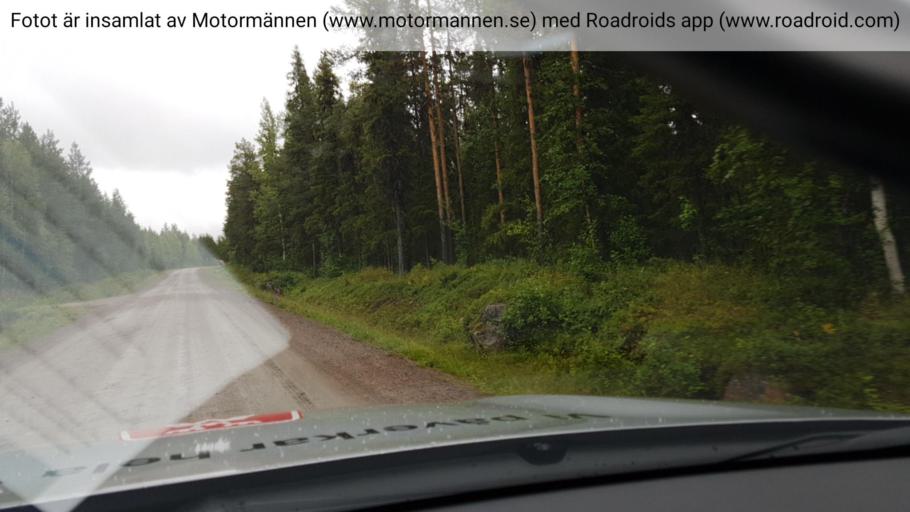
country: SE
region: Norrbotten
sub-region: Gallivare Kommun
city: Gaellivare
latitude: 66.6969
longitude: 20.3753
